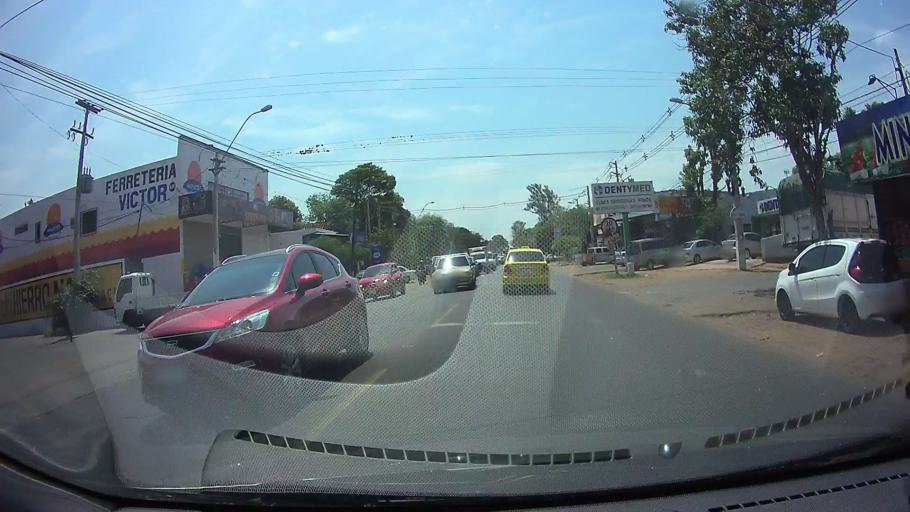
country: PY
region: Central
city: Capiata
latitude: -25.3886
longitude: -57.4705
